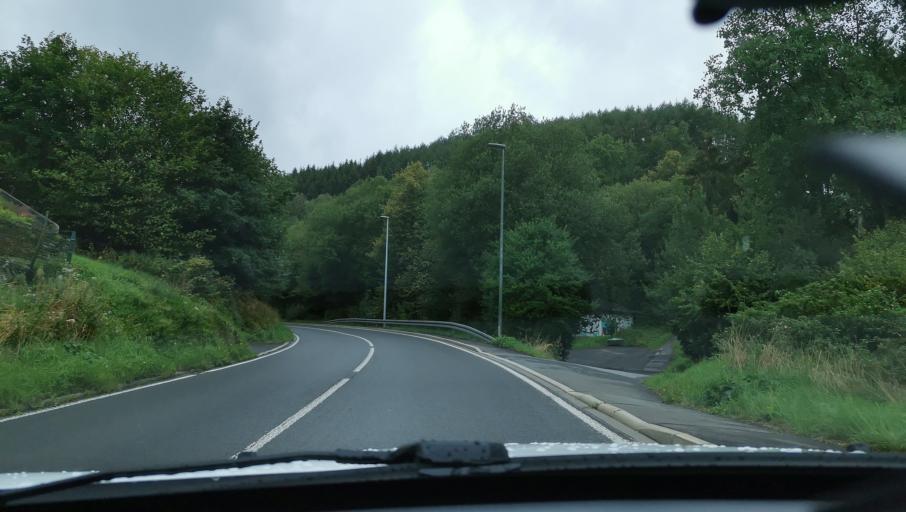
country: DE
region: North Rhine-Westphalia
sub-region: Regierungsbezirk Arnsberg
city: Schalksmuhle
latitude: 51.2085
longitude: 7.5603
